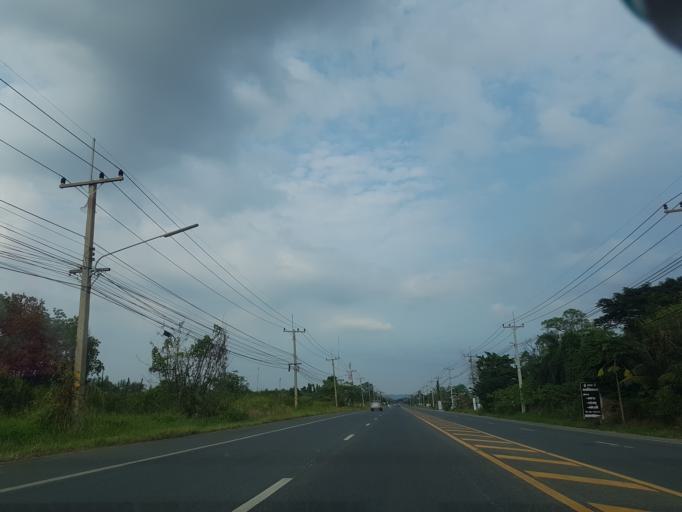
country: TH
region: Sara Buri
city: Phra Phutthabat
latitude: 14.7042
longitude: 100.7811
